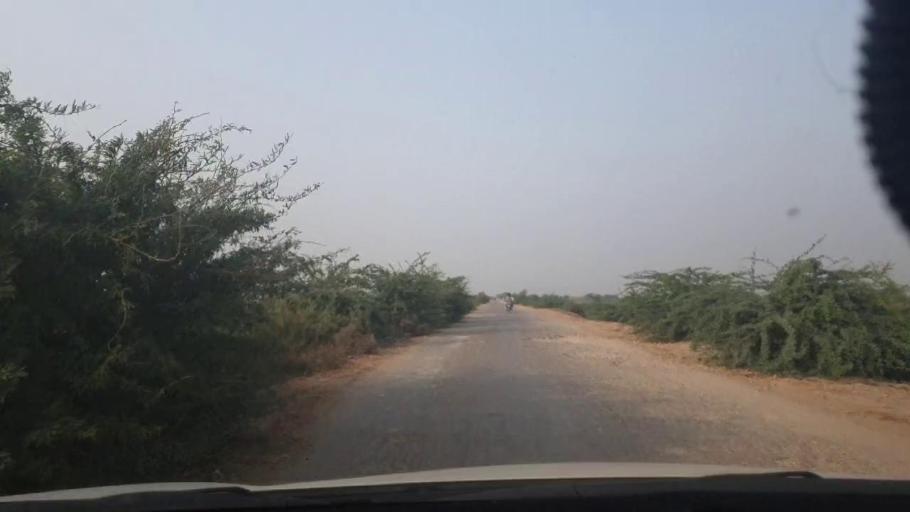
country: PK
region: Sindh
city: Bulri
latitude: 24.7762
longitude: 68.4200
